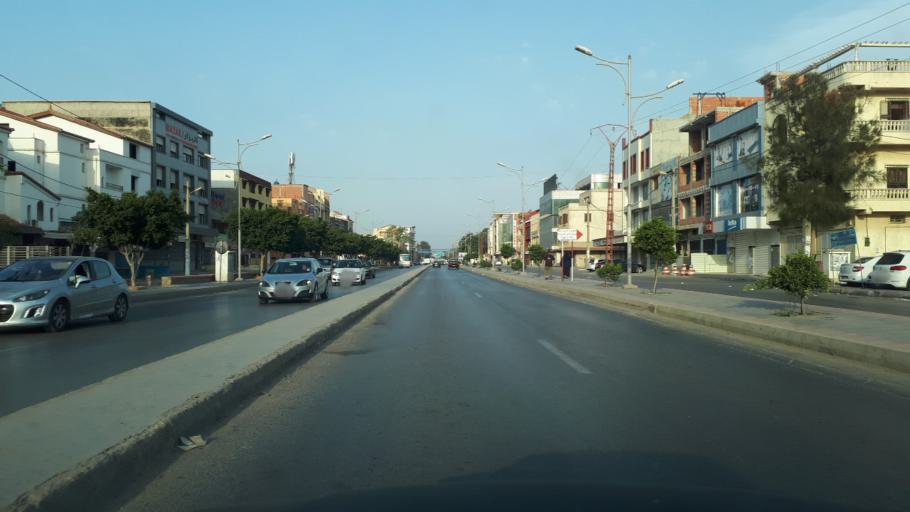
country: DZ
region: Alger
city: Dar el Beida
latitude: 36.7302
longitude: 3.2336
